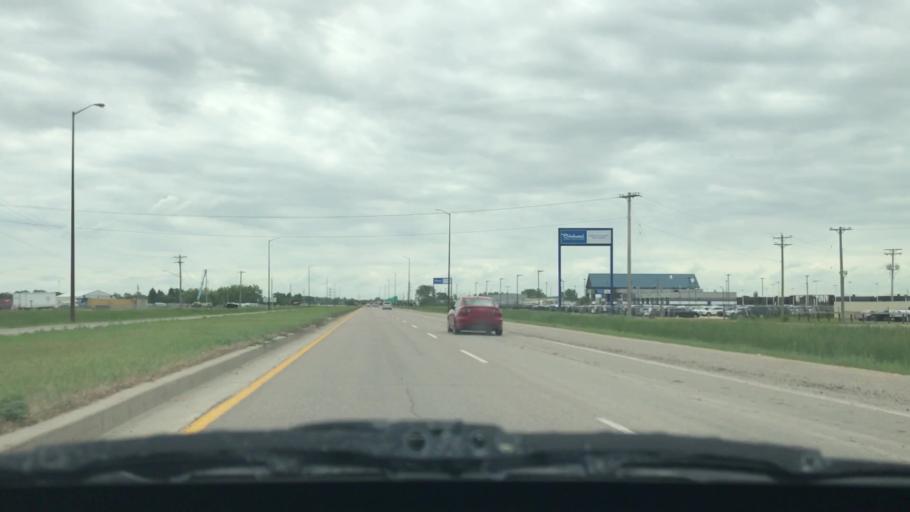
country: CA
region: Manitoba
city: Winnipeg
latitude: 49.8485
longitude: -96.9988
